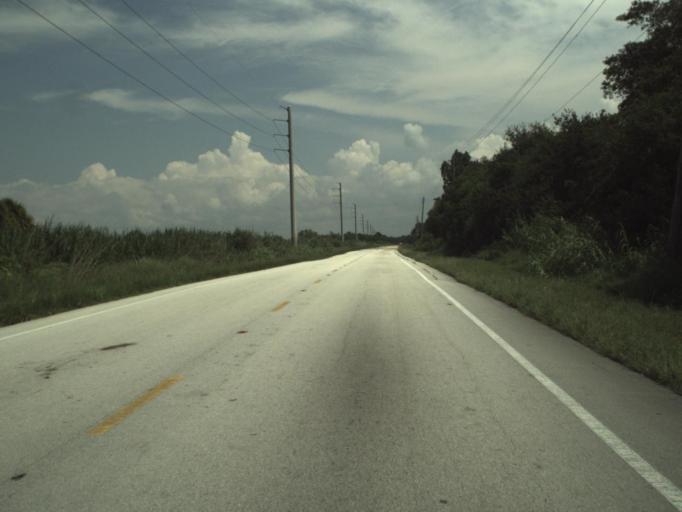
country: US
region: Florida
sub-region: Palm Beach County
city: Pahokee
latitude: 26.9246
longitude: -80.6126
